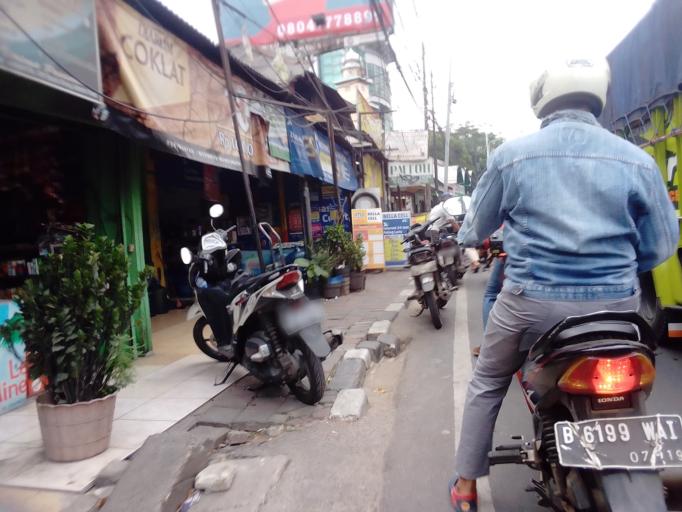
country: ID
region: Jakarta Raya
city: Jakarta
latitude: -6.1981
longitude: 106.8143
